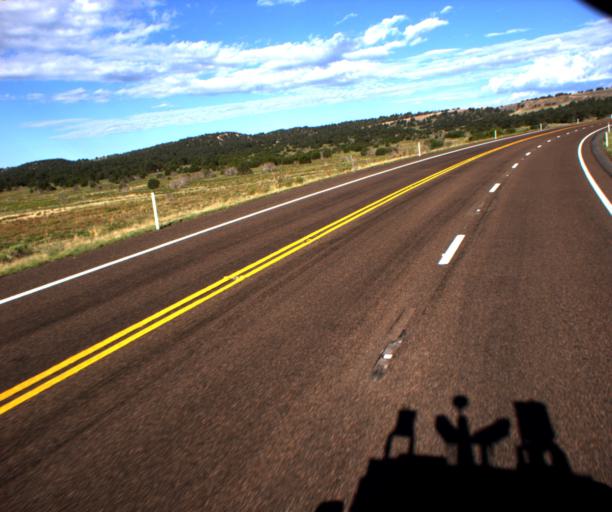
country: US
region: Arizona
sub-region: Apache County
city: Eagar
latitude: 34.0929
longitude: -109.2086
